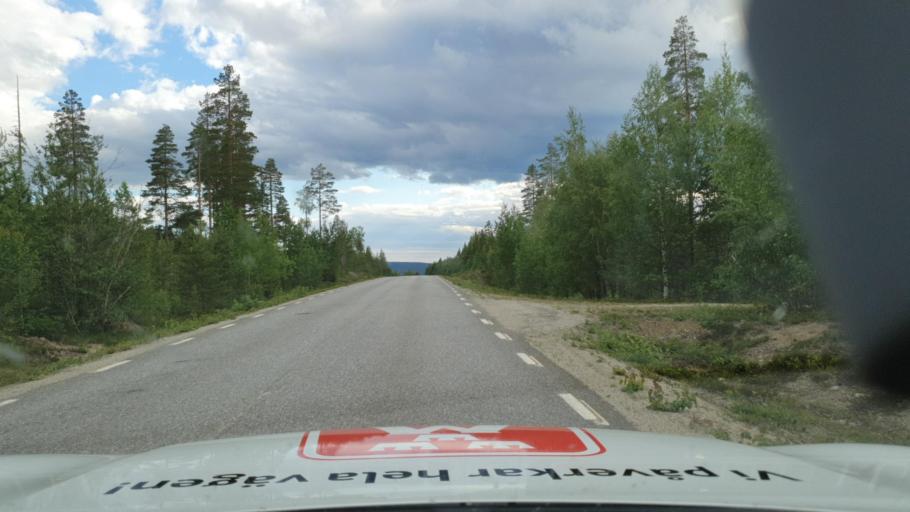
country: SE
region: Vaesterbotten
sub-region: Vindelns Kommun
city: Vindeln
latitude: 64.3491
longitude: 19.6280
